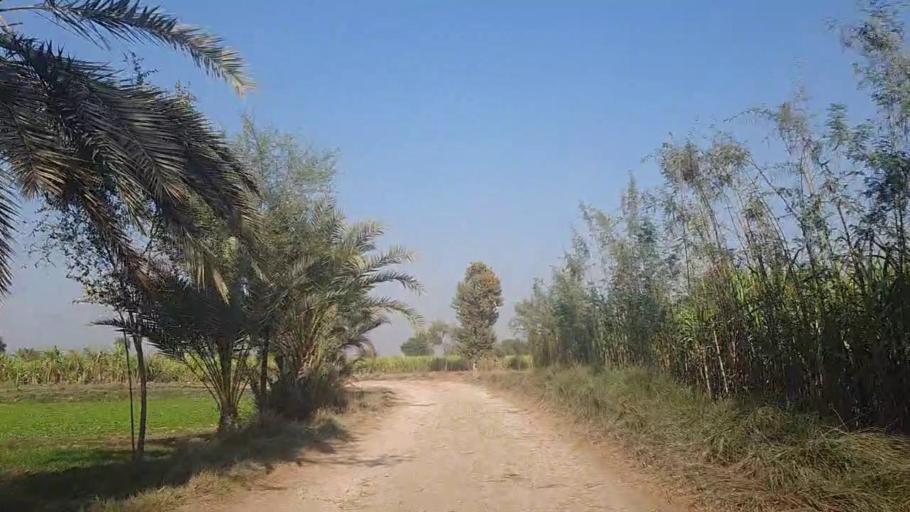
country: PK
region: Sindh
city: Gambat
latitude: 27.3669
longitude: 68.4749
